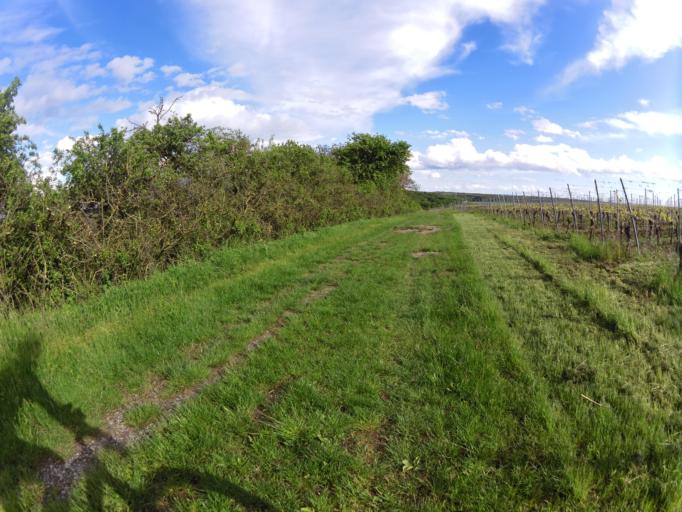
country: DE
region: Bavaria
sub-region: Regierungsbezirk Unterfranken
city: Volkach
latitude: 49.8804
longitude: 10.2662
